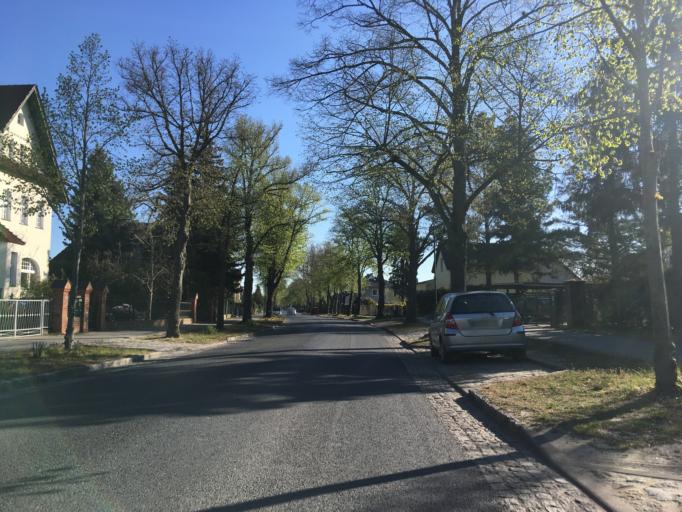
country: DE
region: Berlin
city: Buch
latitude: 52.6682
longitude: 13.5292
